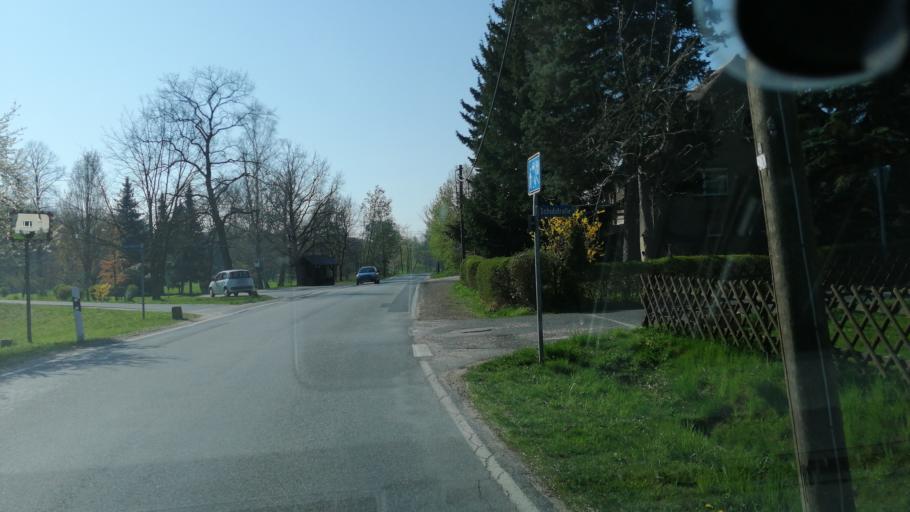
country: DE
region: Saxony
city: Goerlitz
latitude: 51.1769
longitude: 14.9349
